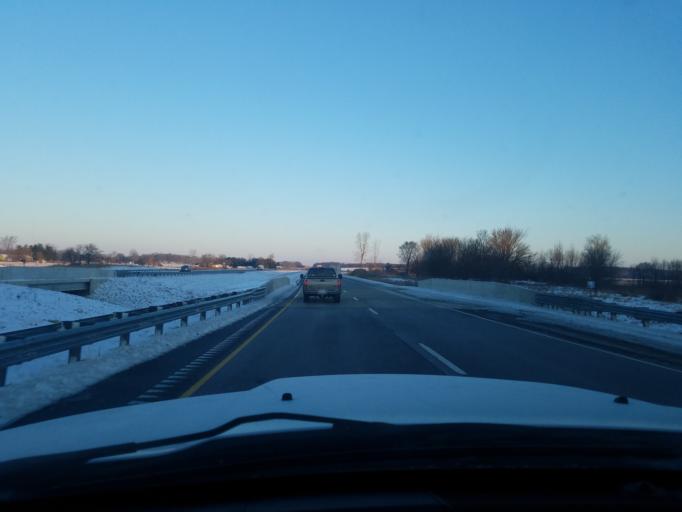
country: US
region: Indiana
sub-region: Marshall County
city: Plymouth
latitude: 41.4081
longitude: -86.2949
